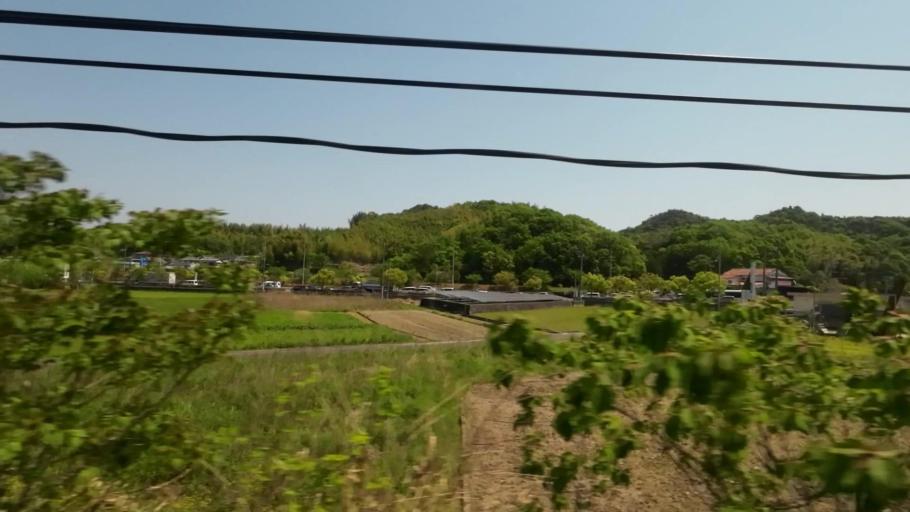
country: JP
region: Ehime
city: Saijo
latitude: 33.9989
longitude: 133.0400
